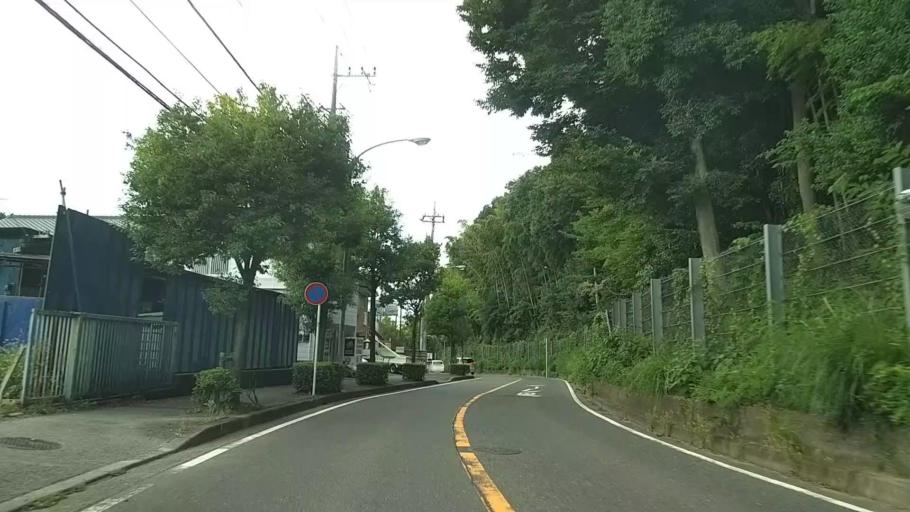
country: JP
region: Kanagawa
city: Yokohama
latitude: 35.5017
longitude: 139.5649
